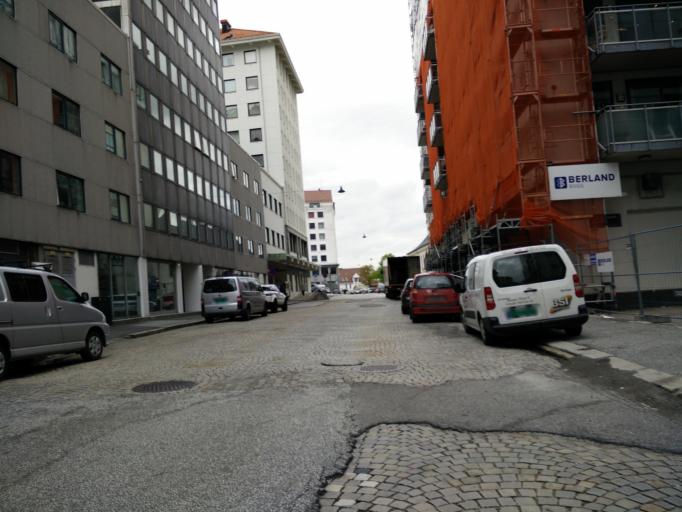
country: NO
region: Hordaland
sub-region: Bergen
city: Bergen
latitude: 60.3980
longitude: 5.3118
